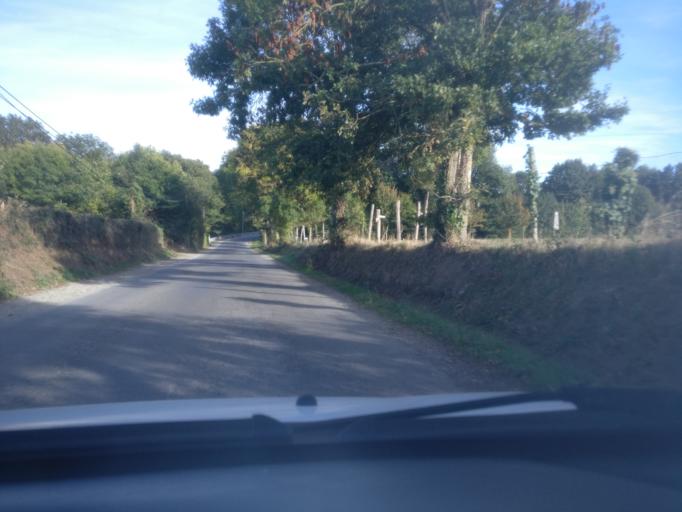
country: FR
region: Lower Normandy
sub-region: Departement de la Manche
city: Sartilly
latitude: 48.7097
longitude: -1.4843
